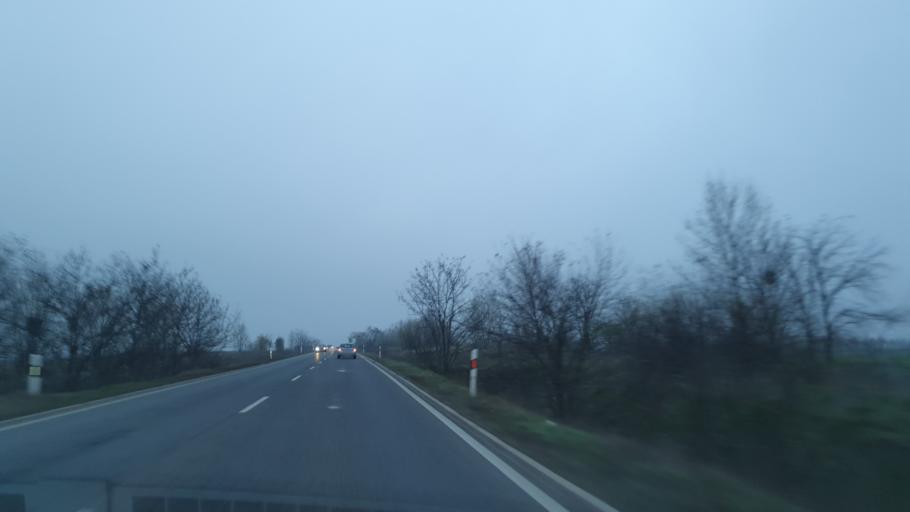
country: HU
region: Pest
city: Csomor
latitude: 47.5497
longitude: 19.1951
